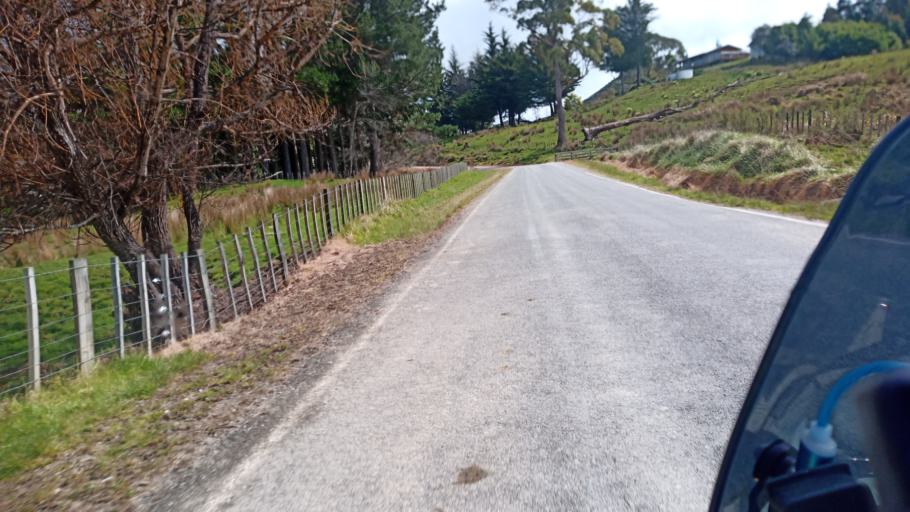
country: NZ
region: Gisborne
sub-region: Gisborne District
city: Gisborne
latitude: -38.5672
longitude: 178.1577
